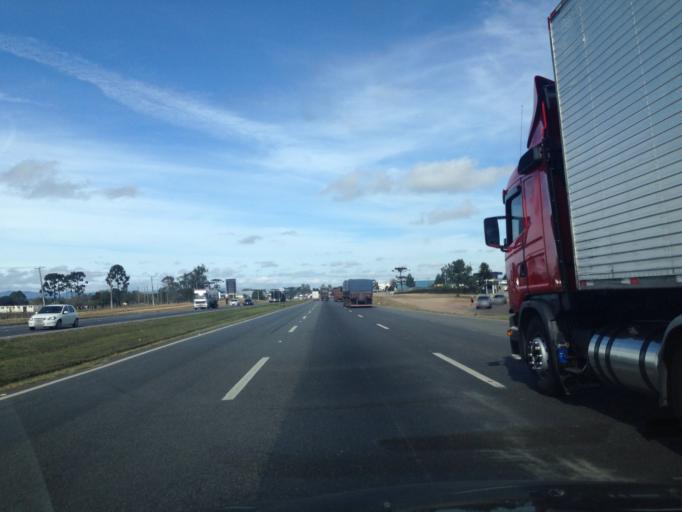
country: BR
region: Parana
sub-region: Sao Jose Dos Pinhais
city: Sao Jose dos Pinhais
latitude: -25.5448
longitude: -49.1508
